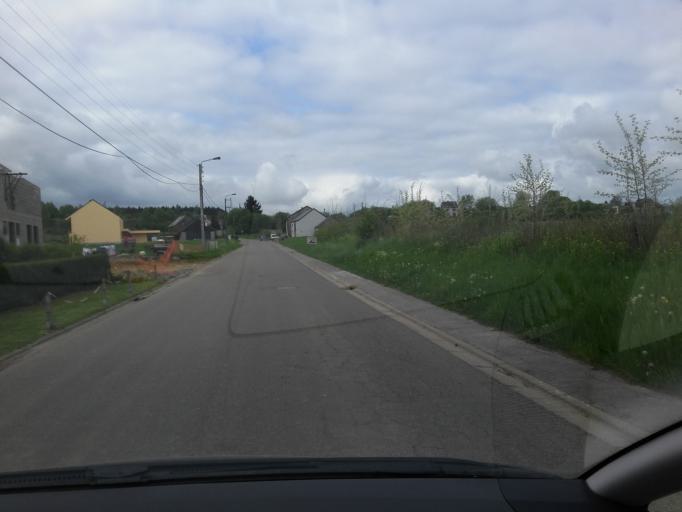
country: BE
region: Wallonia
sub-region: Province du Luxembourg
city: Bertrix
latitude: 49.8171
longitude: 5.3187
